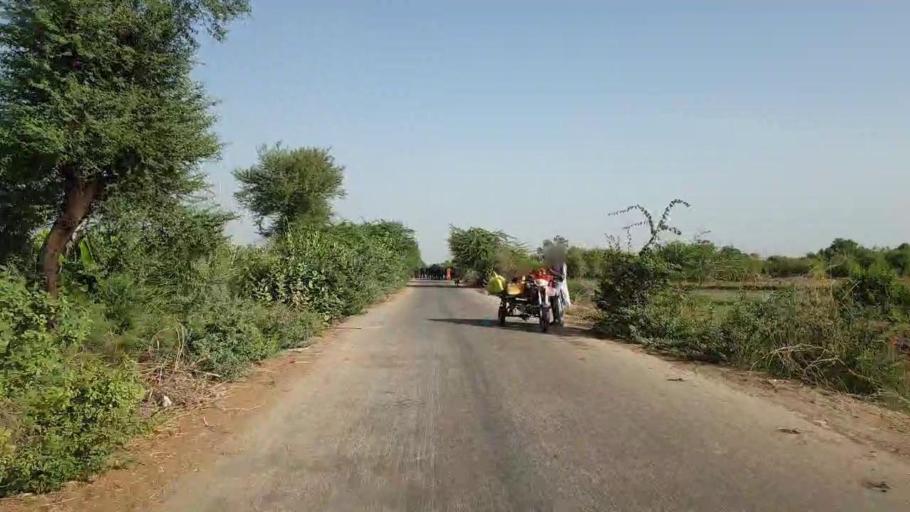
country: PK
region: Sindh
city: Nawabshah
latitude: 26.0909
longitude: 68.4717
